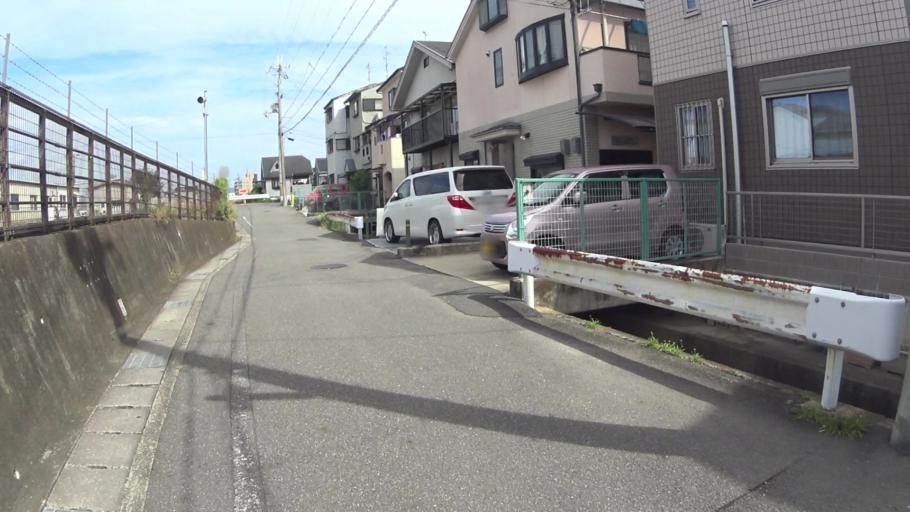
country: JP
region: Kyoto
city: Muko
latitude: 34.9471
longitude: 135.7106
